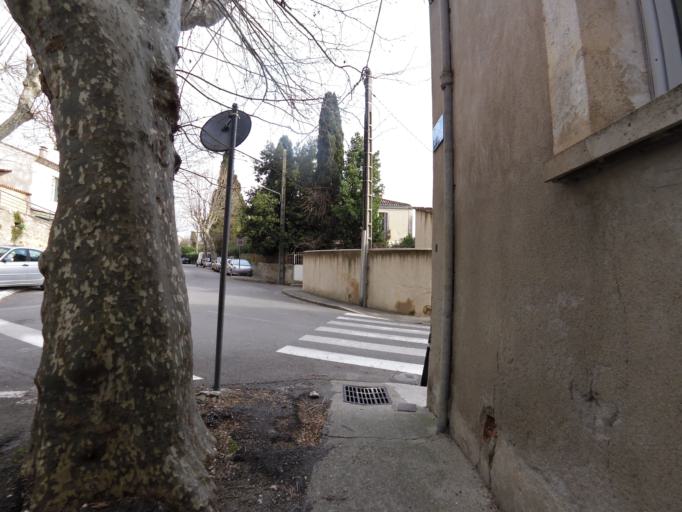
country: FR
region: Languedoc-Roussillon
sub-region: Departement de l'Herault
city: Castries
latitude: 43.6768
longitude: 3.9858
